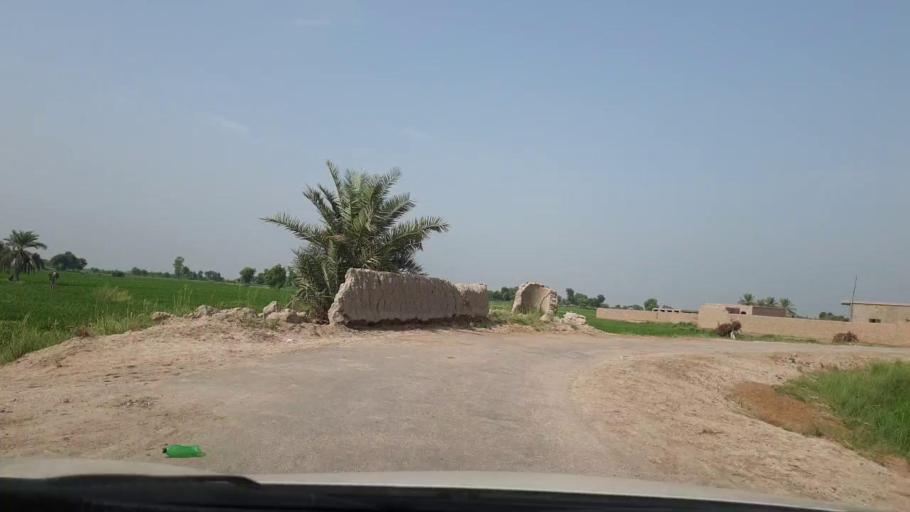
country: PK
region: Sindh
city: Larkana
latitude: 27.4353
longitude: 68.2552
